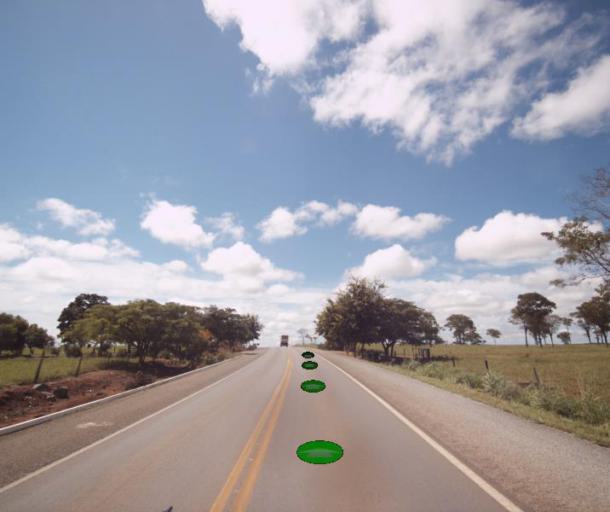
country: BR
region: Goias
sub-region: Padre Bernardo
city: Padre Bernardo
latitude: -15.1635
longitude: -48.3025
